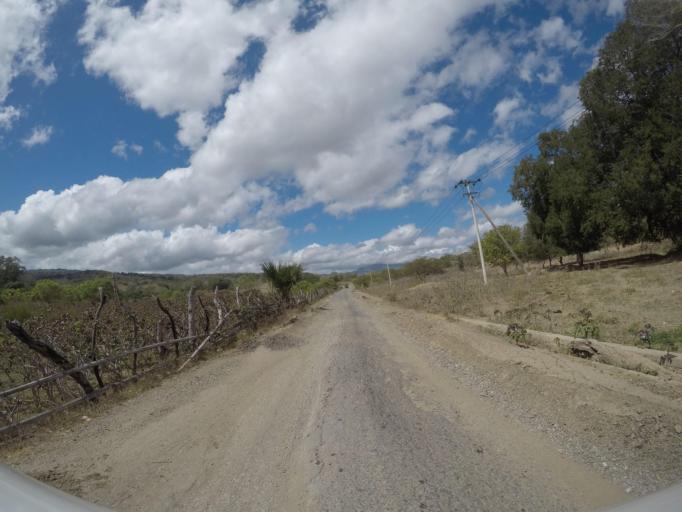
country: TL
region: Lautem
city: Lospalos
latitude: -8.4264
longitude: 126.8312
